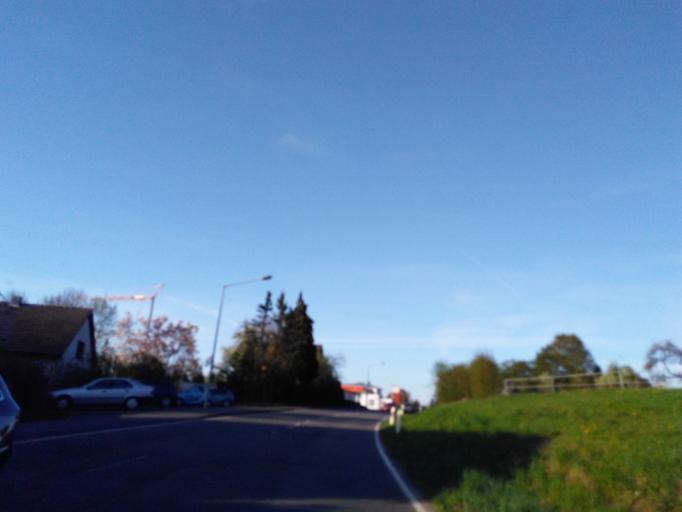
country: DE
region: North Rhine-Westphalia
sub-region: Regierungsbezirk Koln
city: Overath
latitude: 50.8643
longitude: 7.3161
